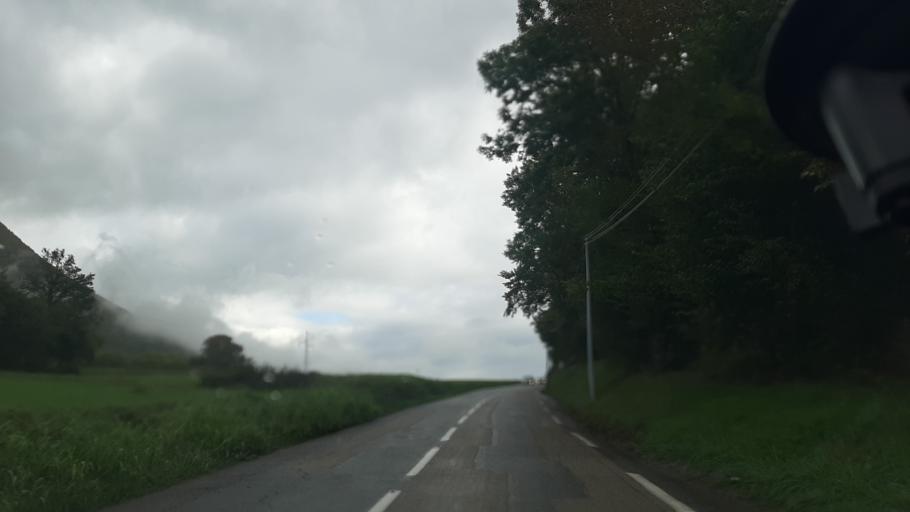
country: FR
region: Rhone-Alpes
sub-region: Departement de la Savoie
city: Gresy-sur-Isere
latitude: 45.6057
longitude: 6.2609
